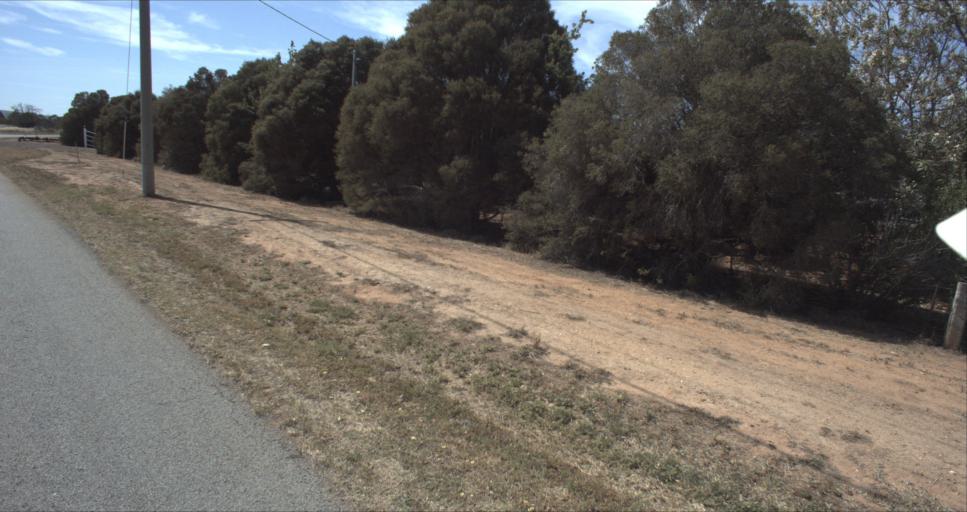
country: AU
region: New South Wales
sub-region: Leeton
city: Leeton
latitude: -34.5718
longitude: 146.4596
